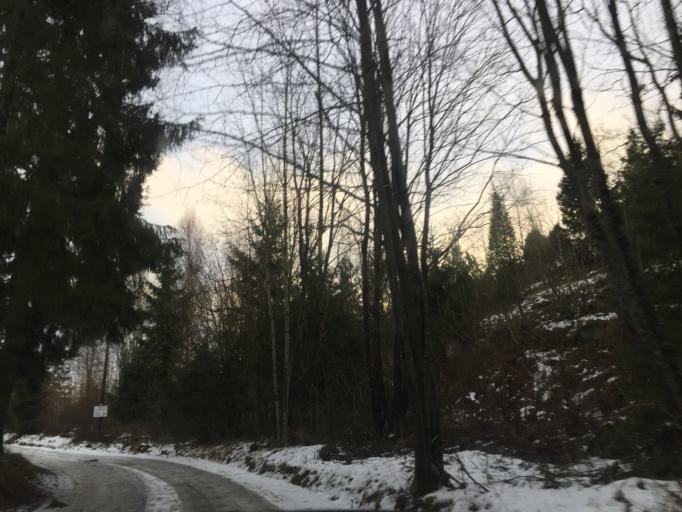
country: NO
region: Ostfold
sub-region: Moss
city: Moss
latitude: 59.4893
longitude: 10.6664
